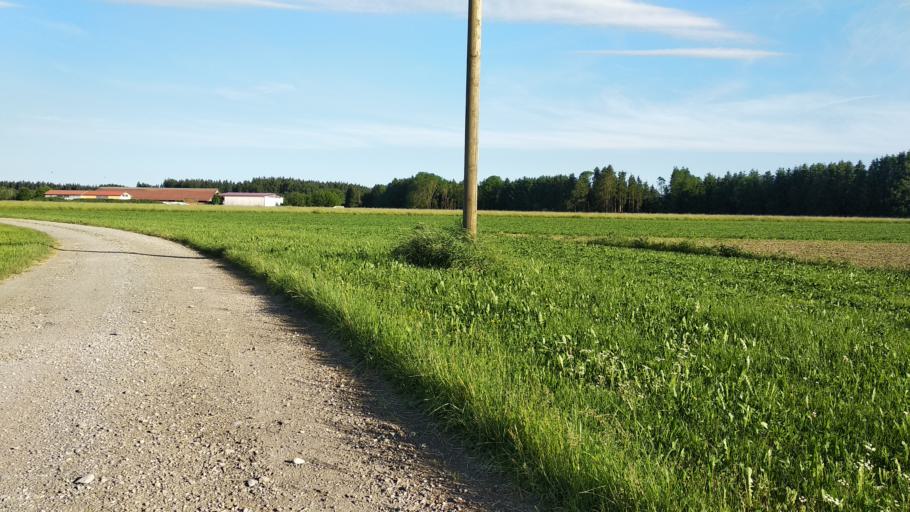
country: DE
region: Bavaria
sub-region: Swabia
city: Lautrach
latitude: 47.9075
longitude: 10.1364
